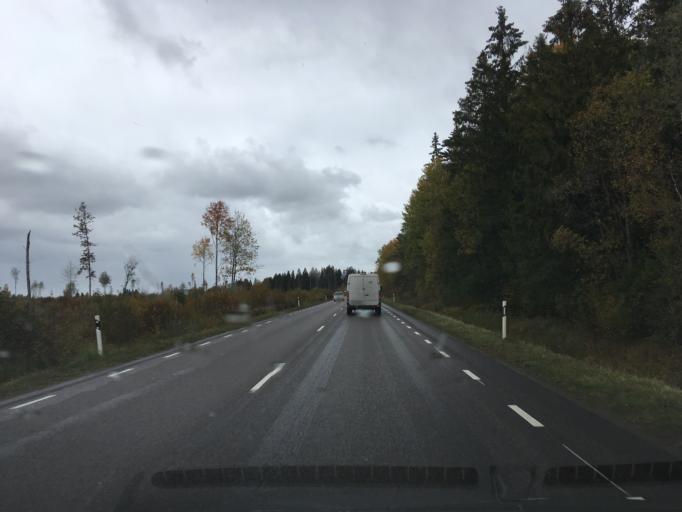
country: EE
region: Harju
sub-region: Anija vald
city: Kehra
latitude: 59.3365
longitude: 25.3114
